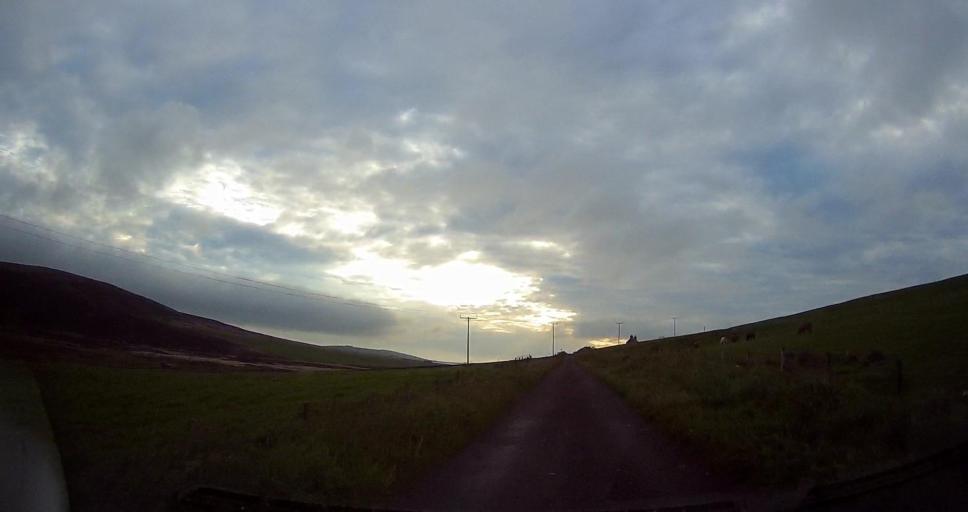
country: GB
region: Scotland
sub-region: Orkney Islands
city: Stromness
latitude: 59.1001
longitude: -3.2044
